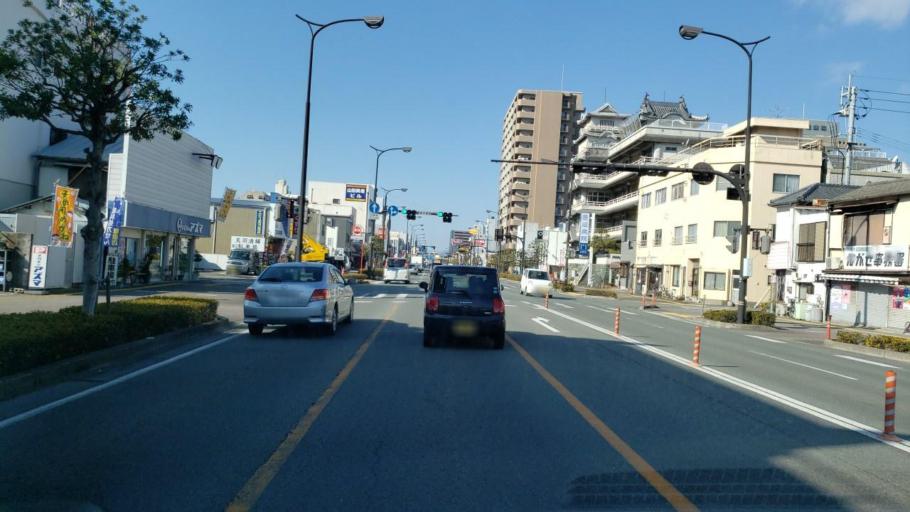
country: JP
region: Tokushima
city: Tokushima-shi
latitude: 34.0780
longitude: 134.5363
